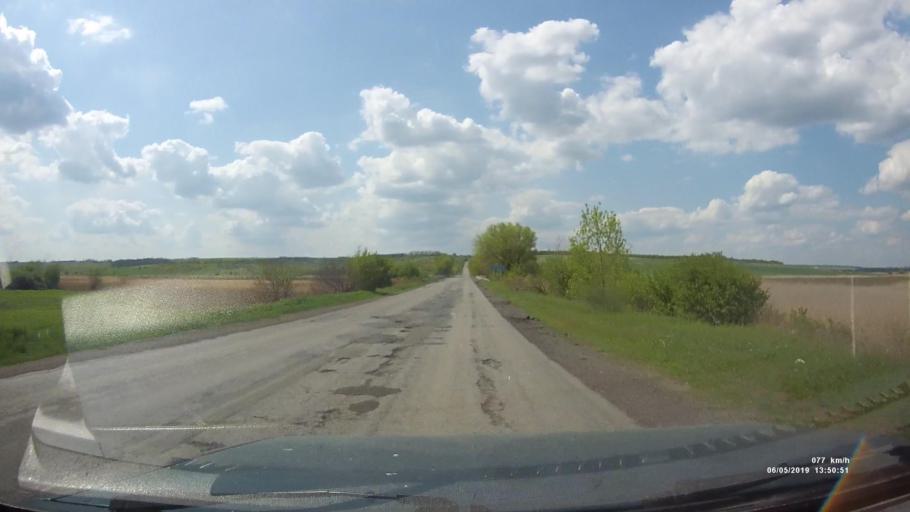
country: RU
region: Rostov
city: Melikhovskaya
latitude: 47.6550
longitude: 40.5019
